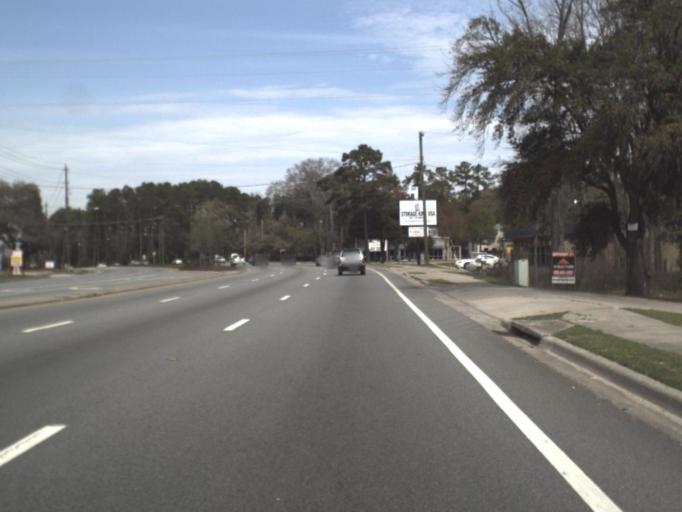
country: US
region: Florida
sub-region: Leon County
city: Tallahassee
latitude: 30.4698
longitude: -84.3611
